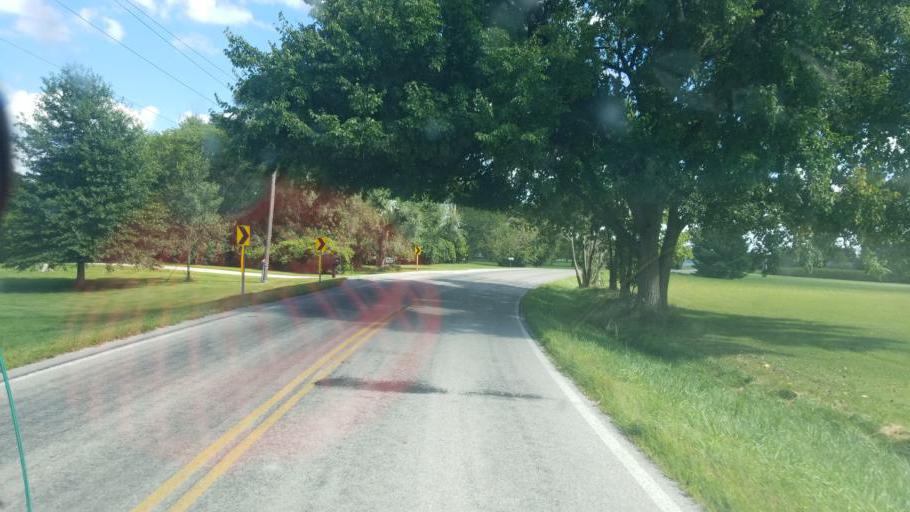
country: US
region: Ohio
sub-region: Marion County
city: Prospect
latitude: 40.3296
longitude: -83.1985
